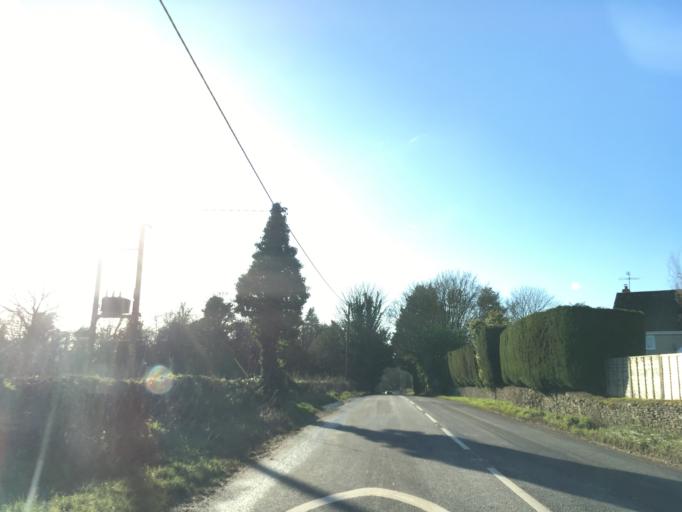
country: GB
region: England
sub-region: Wiltshire
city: Charlton
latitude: 51.5988
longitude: -2.0562
